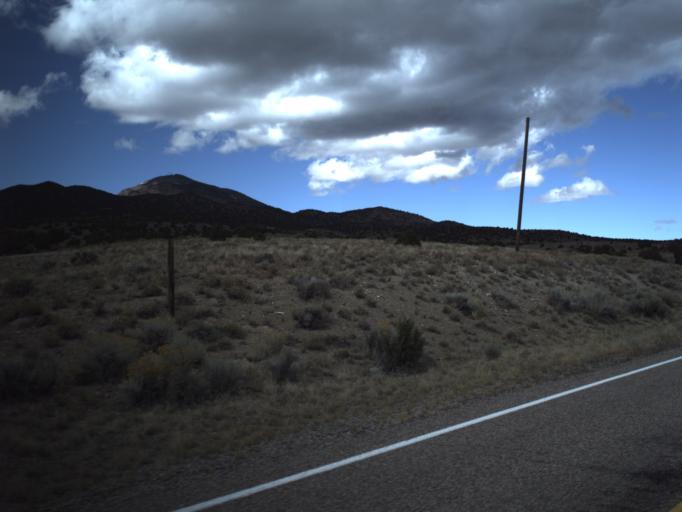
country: US
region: Utah
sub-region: Beaver County
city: Milford
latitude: 38.4481
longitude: -113.2612
